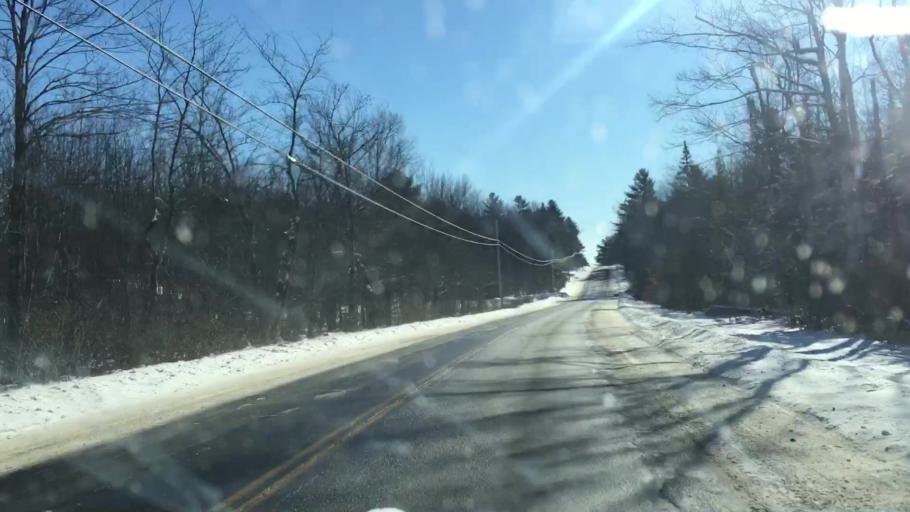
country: US
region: Maine
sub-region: Sagadahoc County
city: Topsham
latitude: 43.9236
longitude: -70.0435
